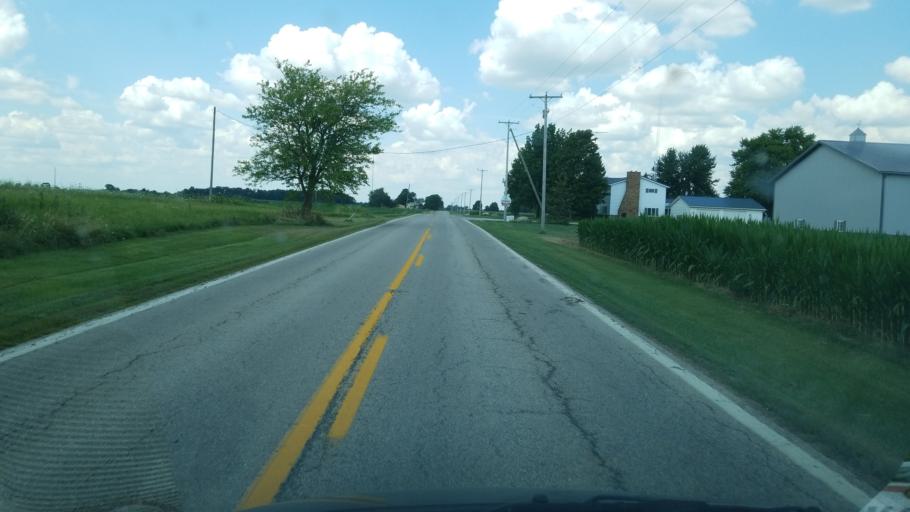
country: US
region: Ohio
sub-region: Union County
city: Richwood
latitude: 40.4313
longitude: -83.4558
